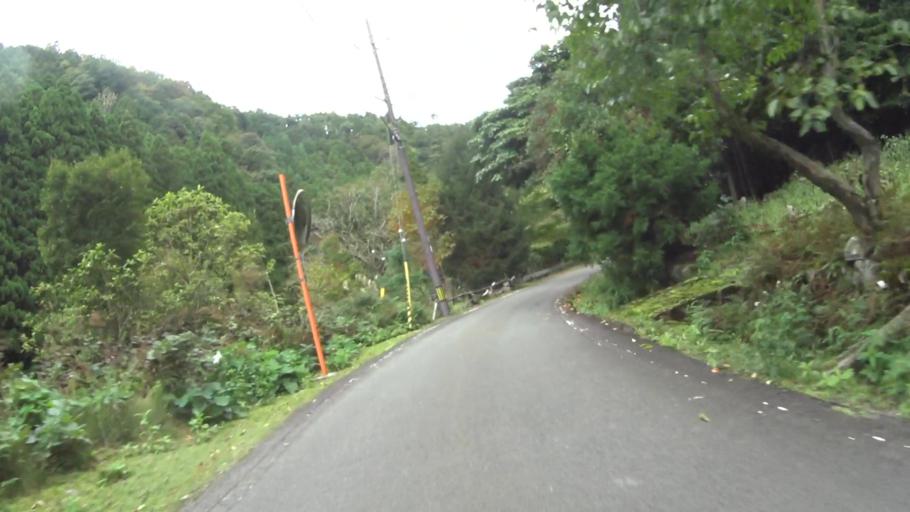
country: JP
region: Fukui
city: Obama
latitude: 35.2927
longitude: 135.6943
